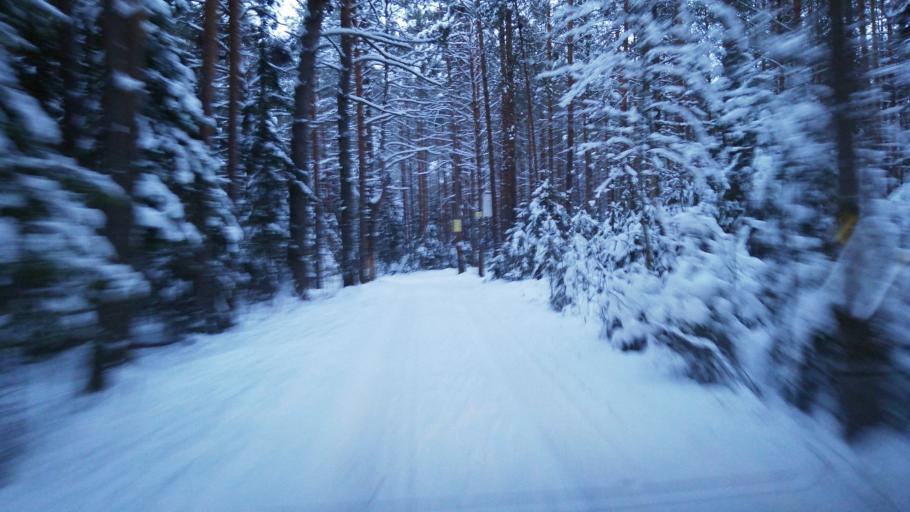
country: RU
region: Jaroslavl
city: Krasnyye Tkachi
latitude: 57.4477
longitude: 39.7966
